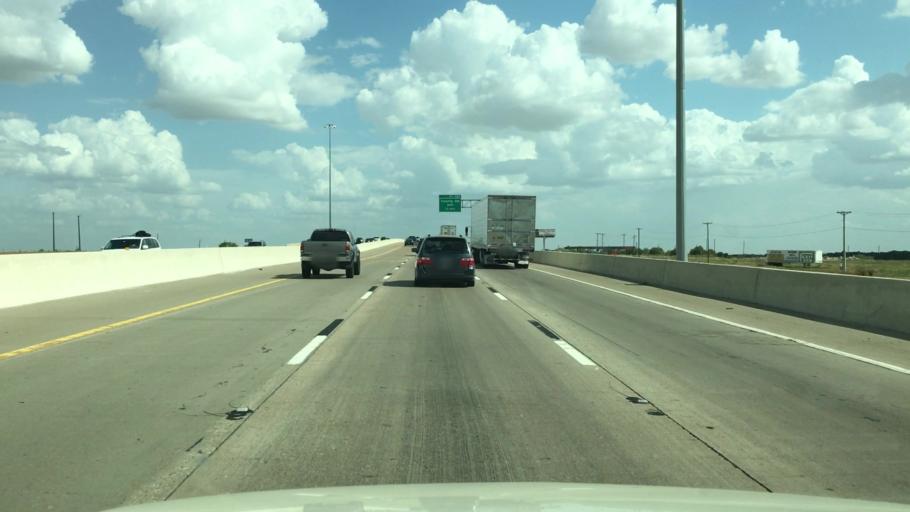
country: US
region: Texas
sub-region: Hill County
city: Hillsboro
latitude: 31.9610
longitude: -97.1172
